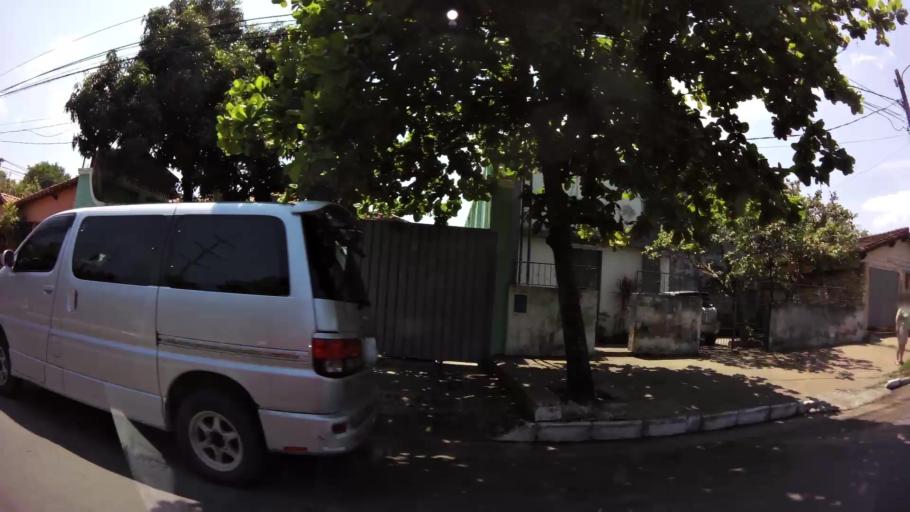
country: PY
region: Asuncion
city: Asuncion
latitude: -25.3047
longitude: -57.6482
